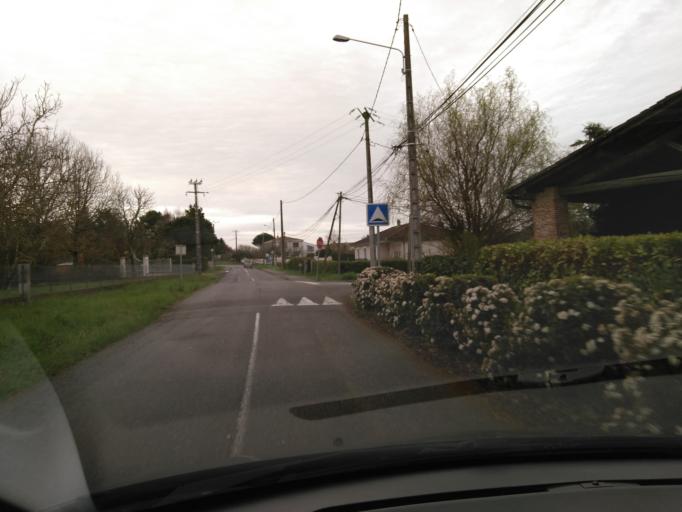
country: FR
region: Midi-Pyrenees
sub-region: Departement de la Haute-Garonne
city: Lapeyrouse-Fossat
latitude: 43.6996
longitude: 1.5114
